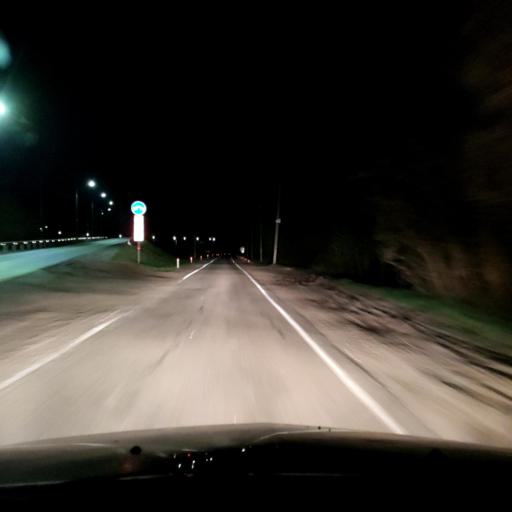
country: RU
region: Voronezj
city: Ramon'
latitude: 52.0073
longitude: 39.2077
